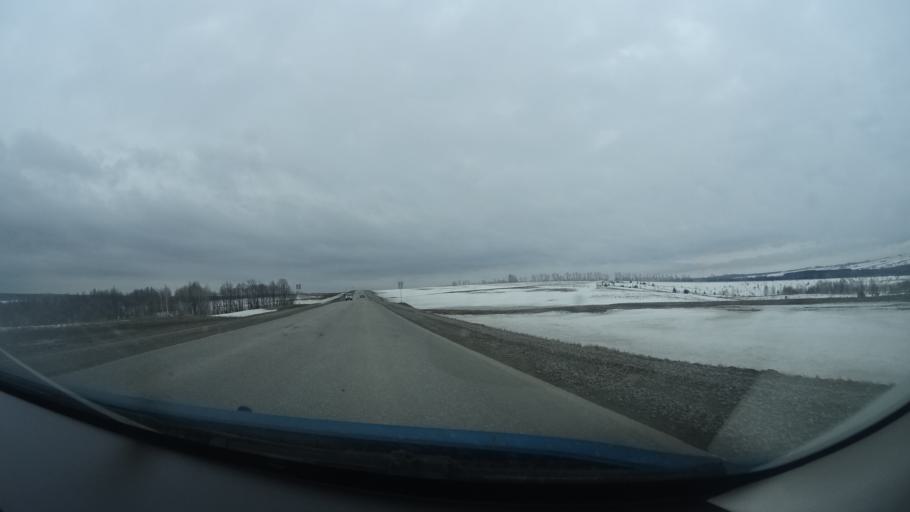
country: RU
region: Bashkortostan
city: Birsk
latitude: 55.3557
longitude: 55.5830
